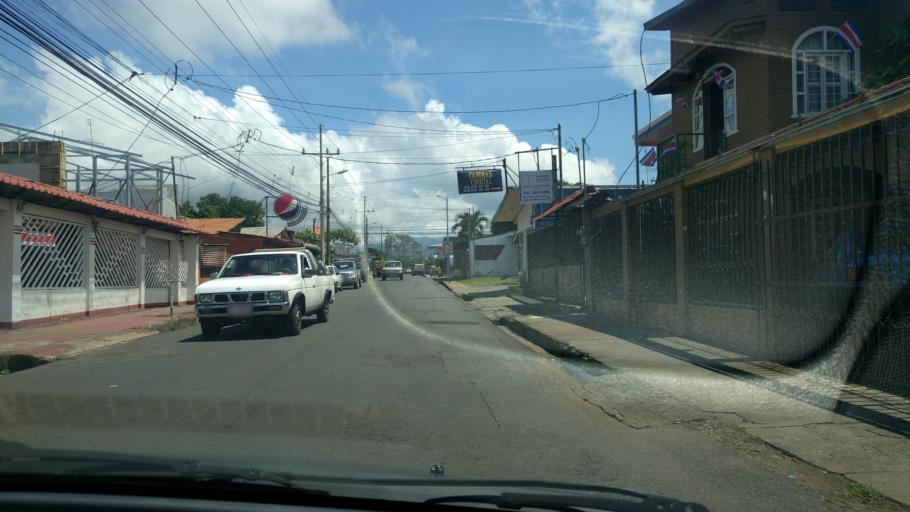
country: CR
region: Puntarenas
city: Esparza
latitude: 9.9918
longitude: -84.6645
